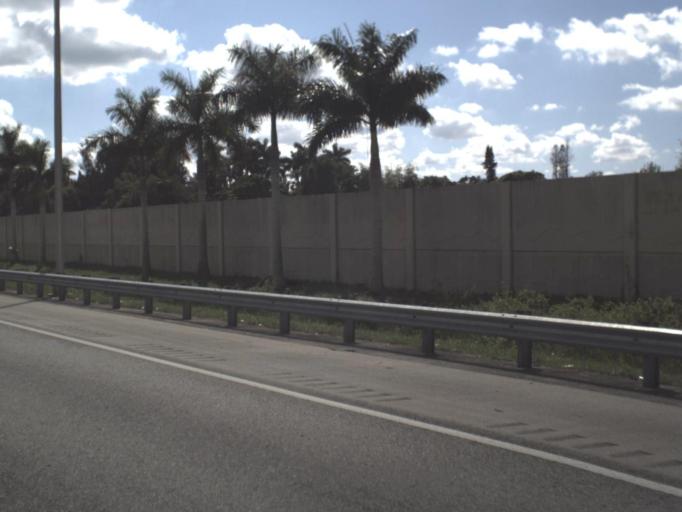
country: US
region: Florida
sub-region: Broward County
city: Lauderhill
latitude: 26.1289
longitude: -80.2179
